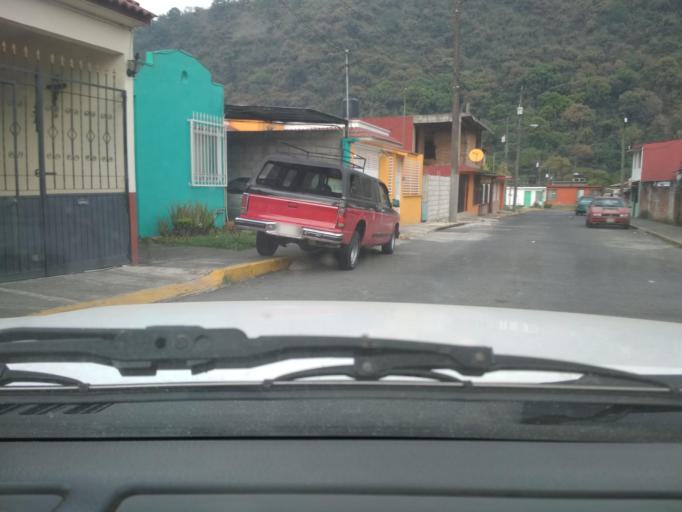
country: MX
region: Veracruz
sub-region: Mariano Escobedo
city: Palmira
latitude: 18.8744
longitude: -97.1013
